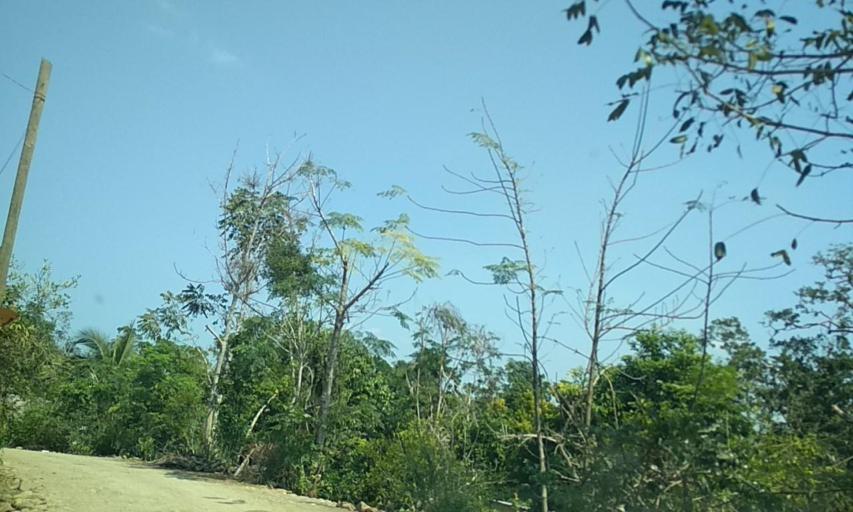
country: MX
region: Veracruz
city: Gutierrez Zamora
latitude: 20.3624
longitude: -97.1663
